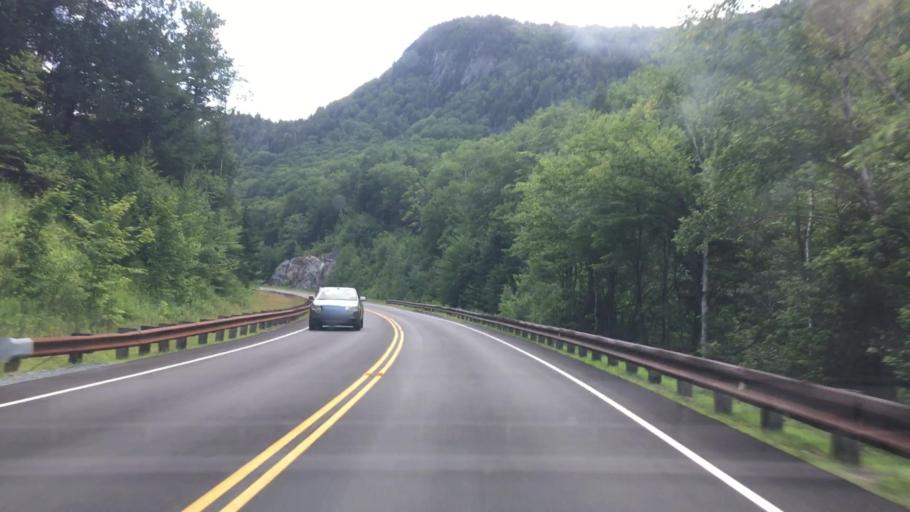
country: US
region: New Hampshire
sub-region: Grafton County
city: Woodstock
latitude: 44.0575
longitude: -71.7936
